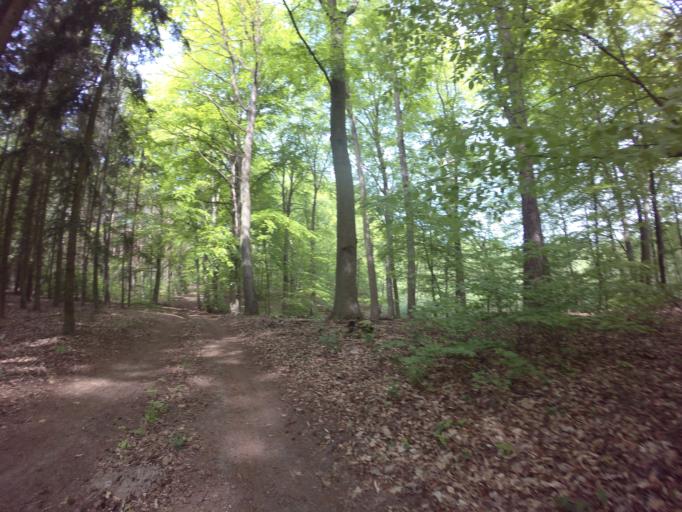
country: PL
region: West Pomeranian Voivodeship
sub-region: Powiat choszczenski
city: Choszczno
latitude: 53.2281
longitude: 15.4102
